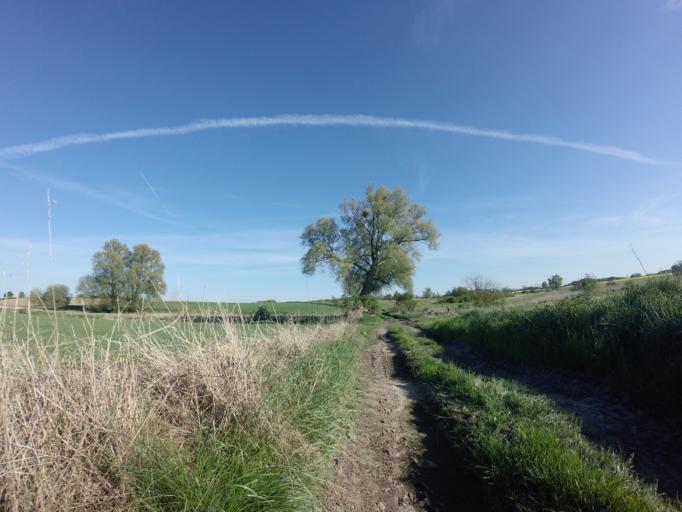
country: PL
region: West Pomeranian Voivodeship
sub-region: Powiat choszczenski
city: Choszczno
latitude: 53.1161
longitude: 15.3548
